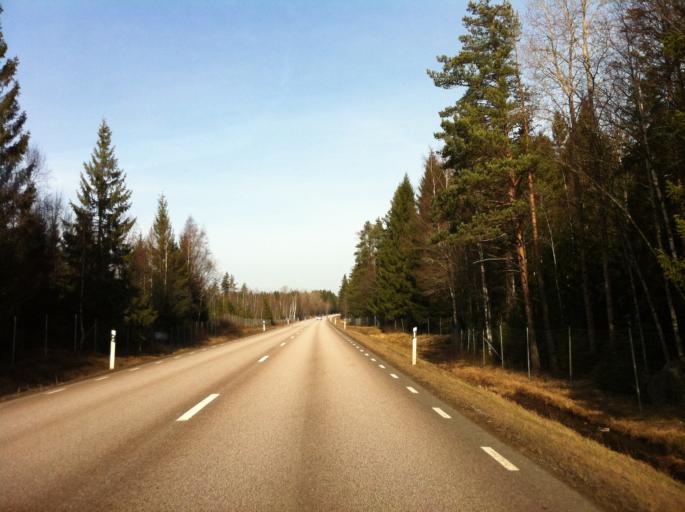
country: SE
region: Vaestra Goetaland
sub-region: Tidaholms Kommun
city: Tidaholm
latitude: 58.0982
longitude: 13.8836
